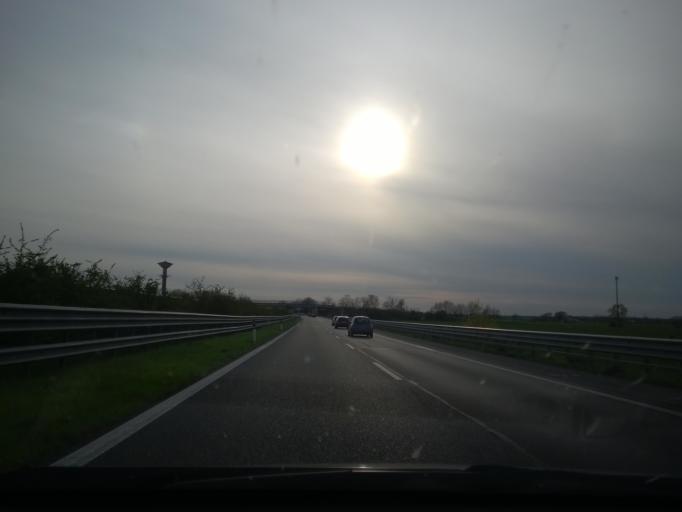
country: IT
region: Emilia-Romagna
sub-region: Provincia di Piacenza
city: Caorso
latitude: 45.0527
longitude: 9.8688
